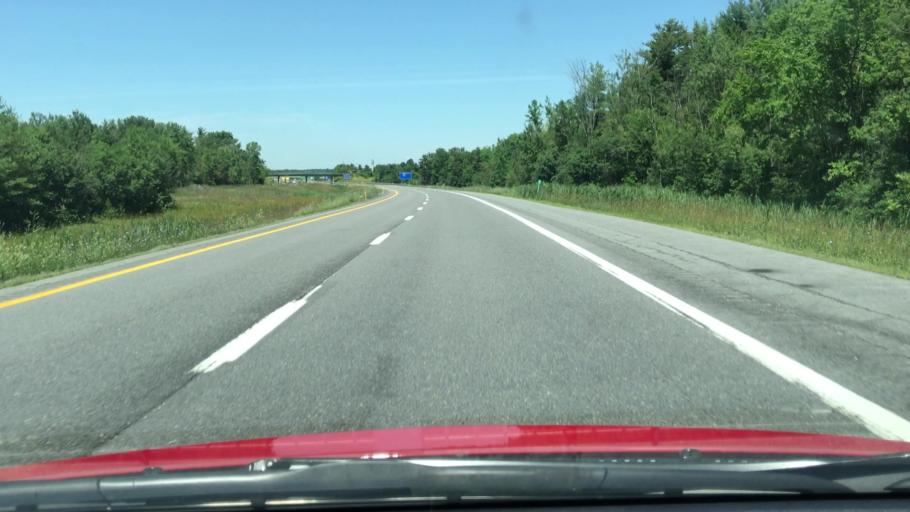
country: US
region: New York
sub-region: Clinton County
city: Champlain
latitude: 44.9674
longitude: -73.4500
